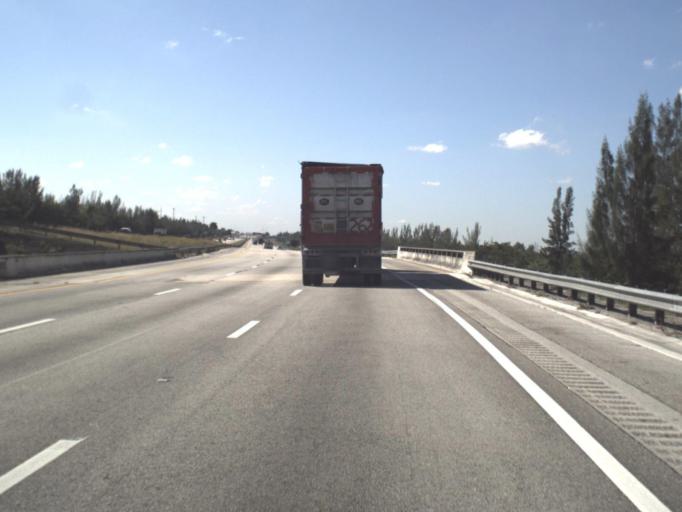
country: US
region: Florida
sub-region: Miami-Dade County
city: Palm Springs North
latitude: 25.9284
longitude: -80.3753
